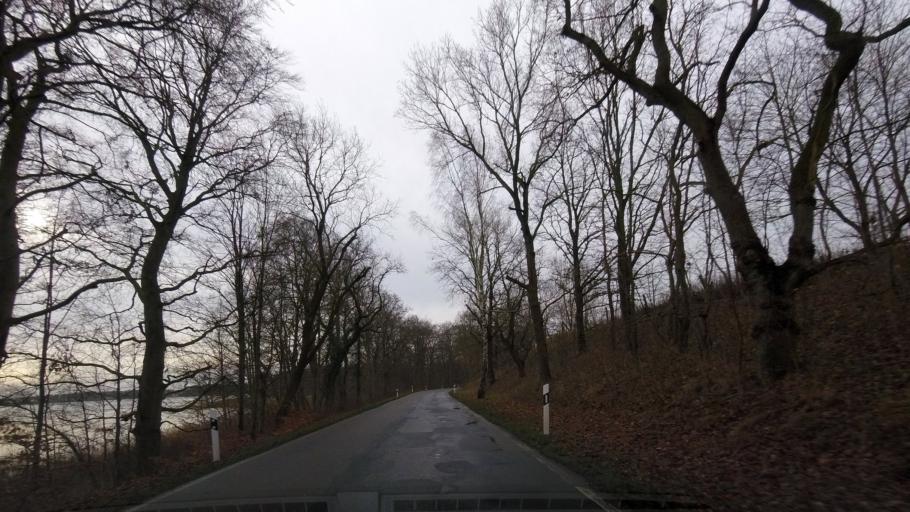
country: DE
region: Mecklenburg-Vorpommern
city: Waren
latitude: 53.5361
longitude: 12.6867
